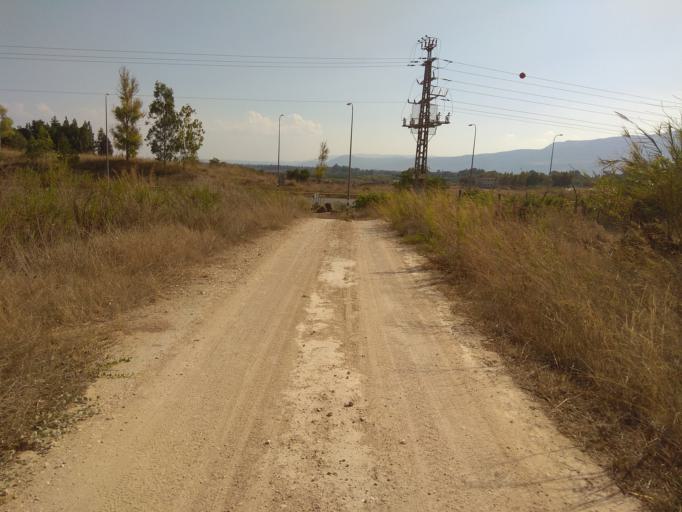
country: IL
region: Northern District
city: Qiryat Shemona
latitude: 33.2245
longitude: 35.6181
